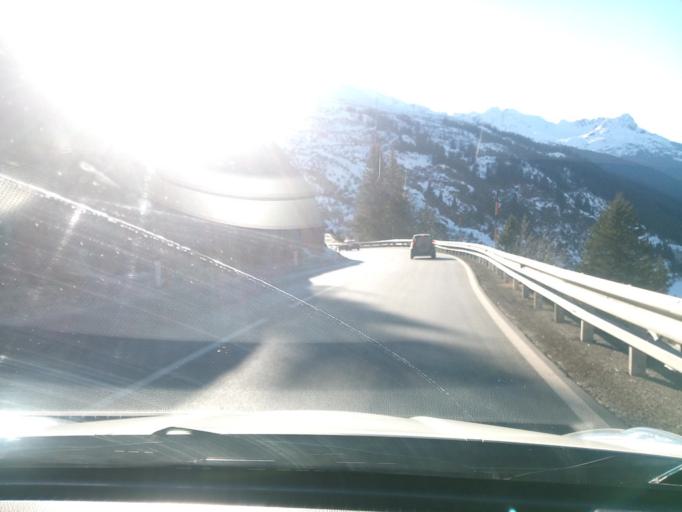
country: AT
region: Vorarlberg
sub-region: Politischer Bezirk Bludenz
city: Lech
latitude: 47.1404
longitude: 10.1652
